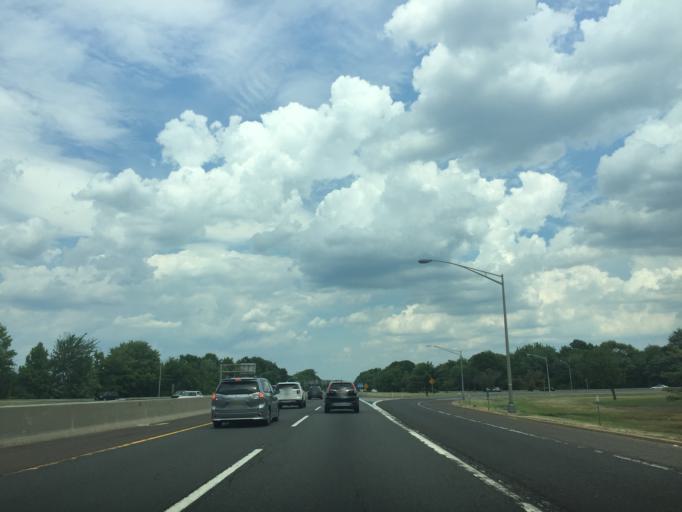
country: US
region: New Jersey
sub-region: Burlington County
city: Ramblewood
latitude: 39.9312
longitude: -74.9529
